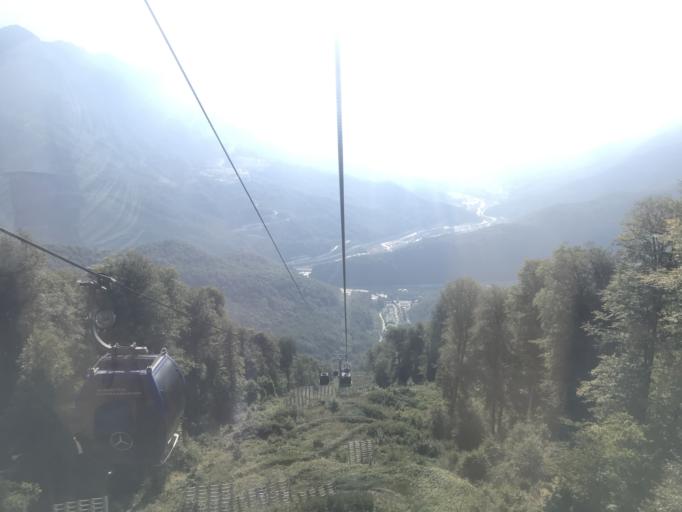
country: RU
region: Krasnodarskiy
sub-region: Sochi City
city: Krasnaya Polyana
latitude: 43.6922
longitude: 40.3089
